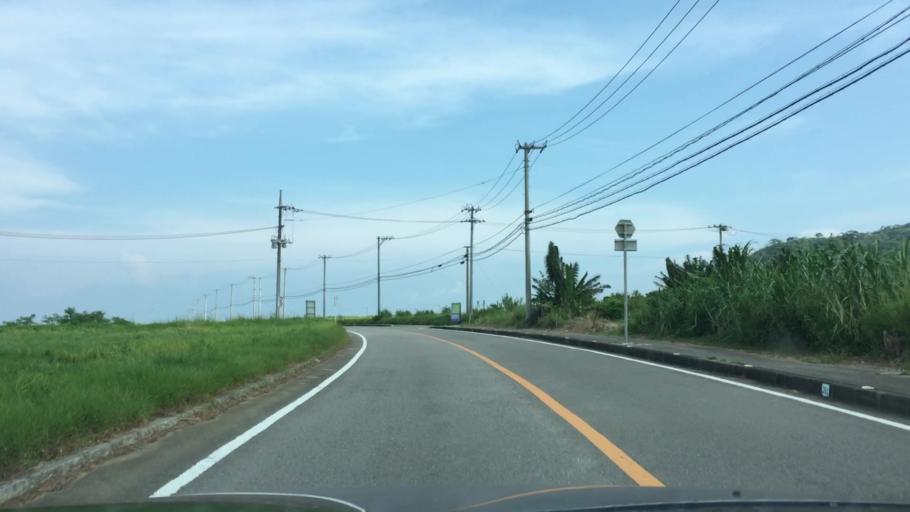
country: JP
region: Okinawa
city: Ishigaki
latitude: 24.5070
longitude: 124.2709
